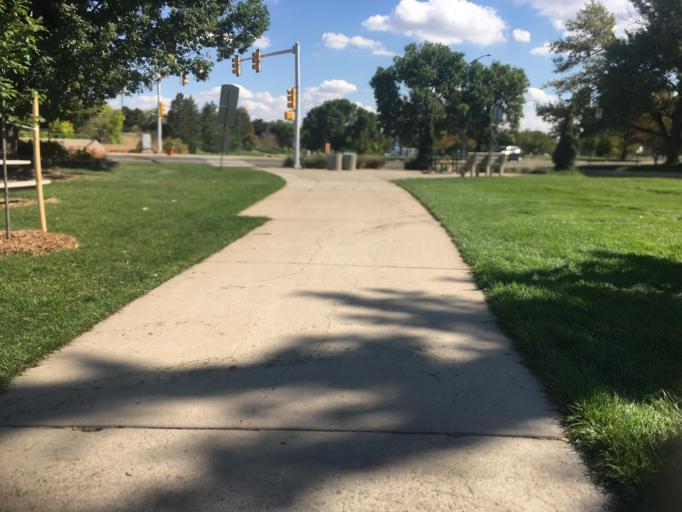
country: US
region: Colorado
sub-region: Broomfield County
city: Broomfield
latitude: 39.9202
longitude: -105.0723
